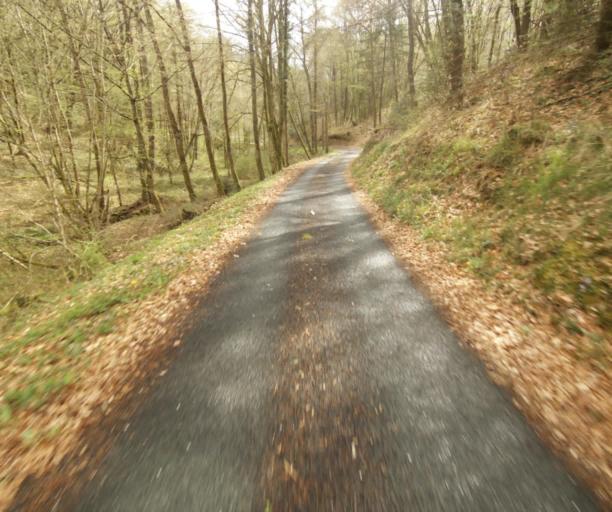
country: FR
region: Limousin
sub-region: Departement de la Correze
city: Tulle
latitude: 45.2833
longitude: 1.7371
